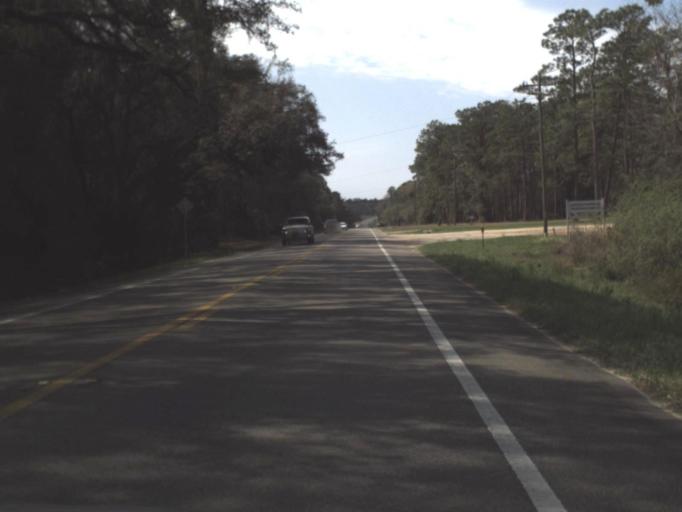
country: US
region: Florida
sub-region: Gadsden County
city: Gretna
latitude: 30.5388
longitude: -84.7621
